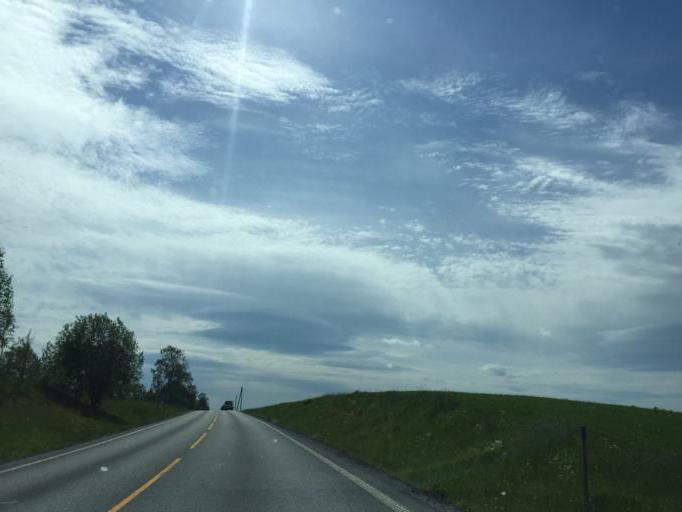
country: NO
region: Akershus
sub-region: Nes
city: Arnes
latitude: 60.1486
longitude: 11.4210
